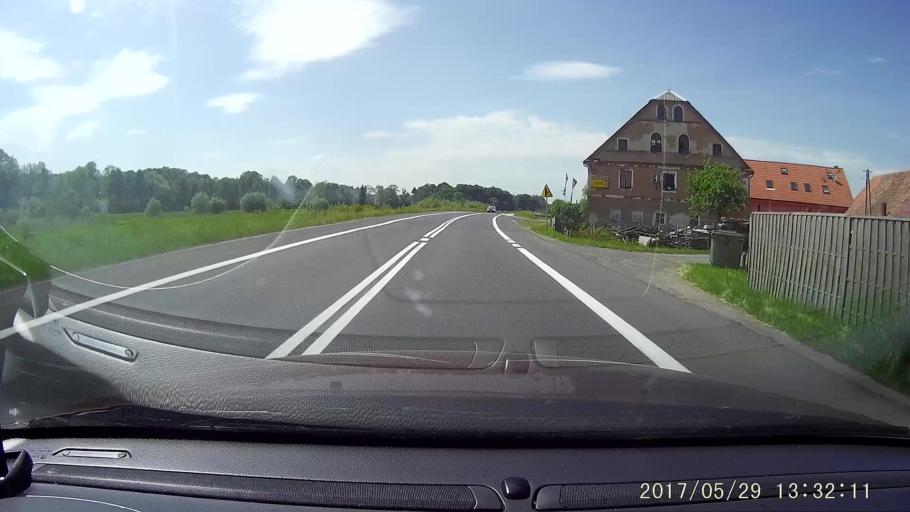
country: PL
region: Lower Silesian Voivodeship
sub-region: Powiat lubanski
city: Olszyna
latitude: 51.0830
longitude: 15.3291
